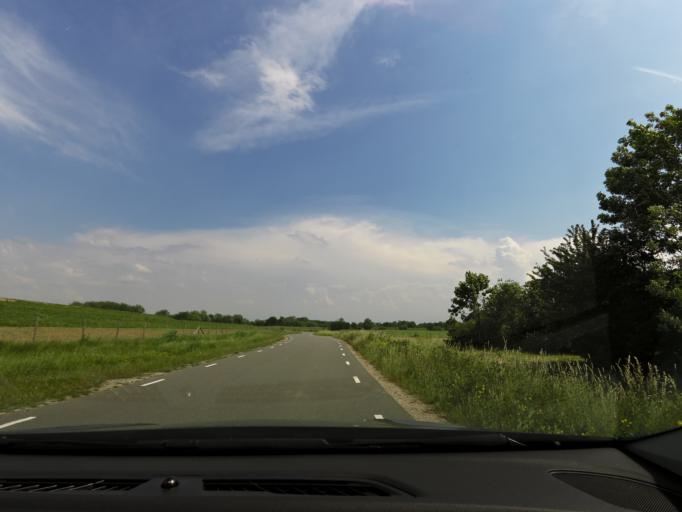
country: NL
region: North Brabant
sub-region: Gemeente Woudrichem
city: Woudrichem
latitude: 51.8005
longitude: 5.0523
